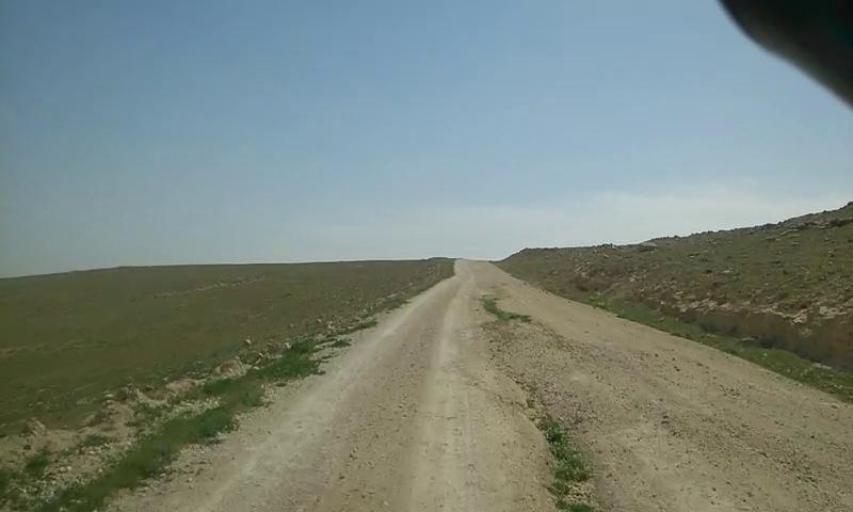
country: PS
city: `Arab ar Rashaydah
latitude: 31.5212
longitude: 35.2971
